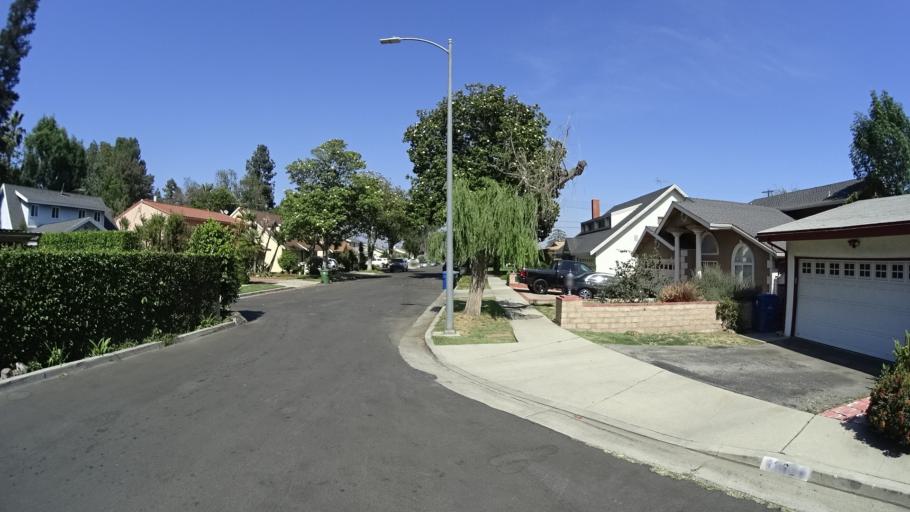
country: US
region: California
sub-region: Los Angeles County
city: Van Nuys
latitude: 34.1984
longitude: -118.4300
